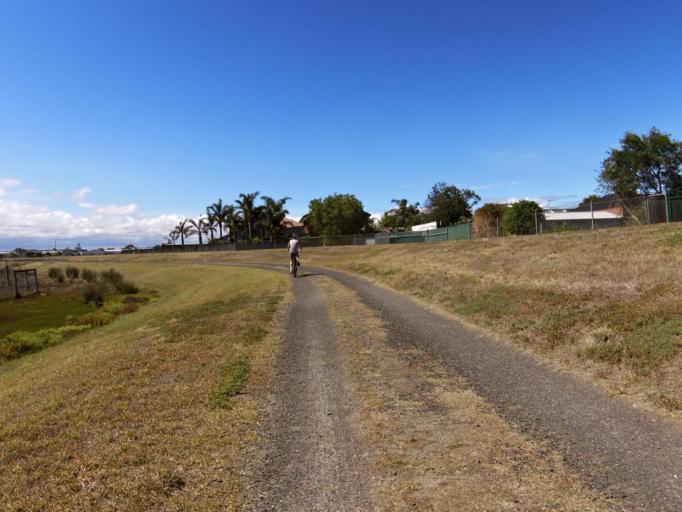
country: AU
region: Victoria
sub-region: Hobsons Bay
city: Altona
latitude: -37.8685
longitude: 144.8051
